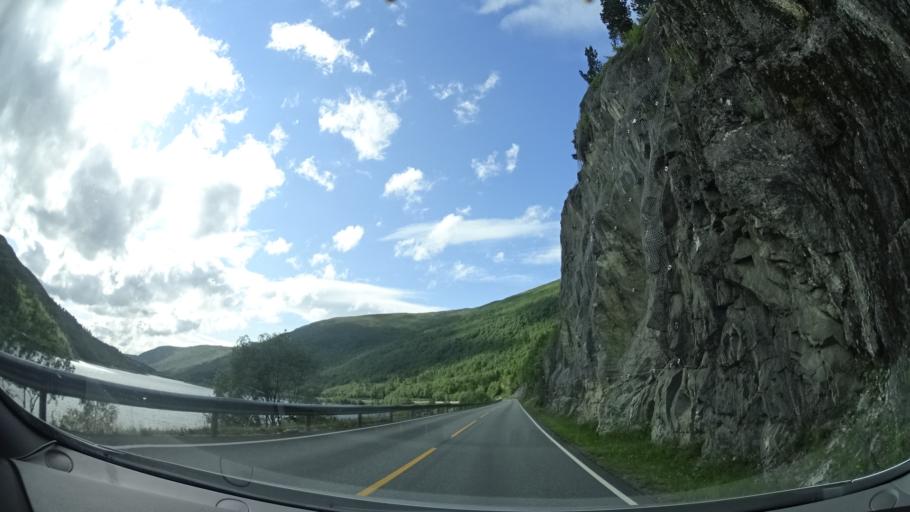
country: NO
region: More og Romsdal
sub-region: Rindal
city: Rindal
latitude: 63.2214
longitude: 9.2614
